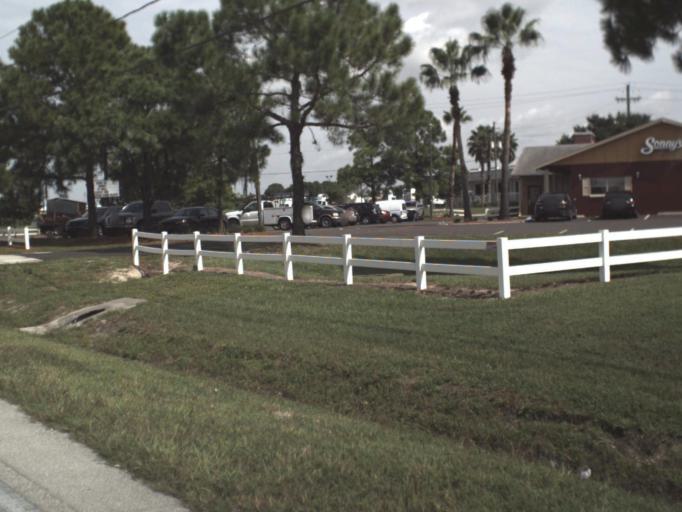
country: US
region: Florida
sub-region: Polk County
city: Jan-Phyl Village
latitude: 28.0286
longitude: -81.7787
